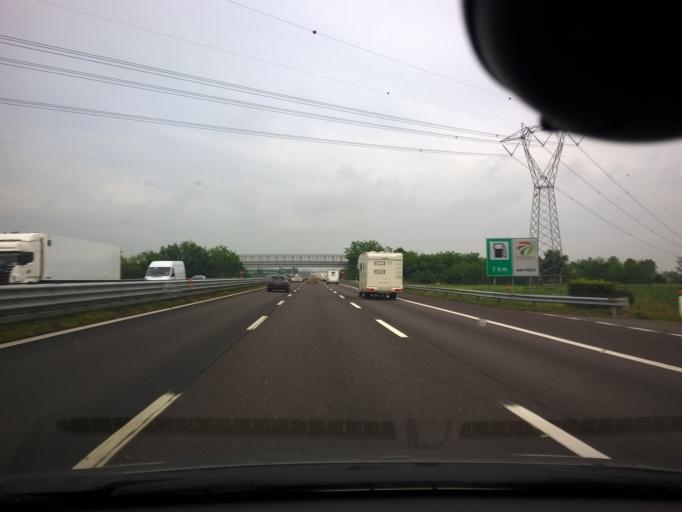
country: IT
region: Lombardy
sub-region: Provincia di Brescia
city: Calcinato
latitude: 45.4610
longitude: 10.4413
